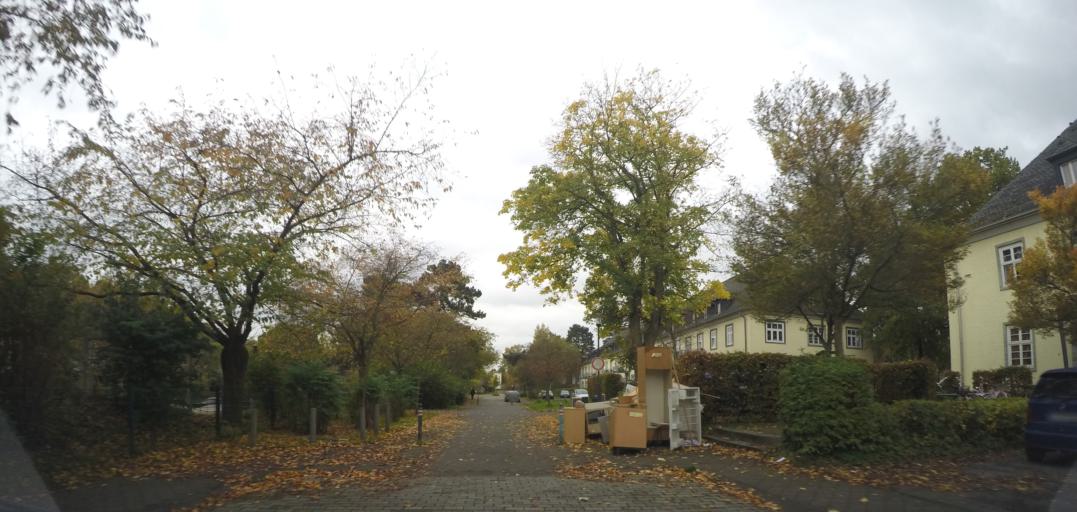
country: DE
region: North Rhine-Westphalia
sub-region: Regierungsbezirk Arnsberg
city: Lippstadt
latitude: 51.6602
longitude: 8.3499
